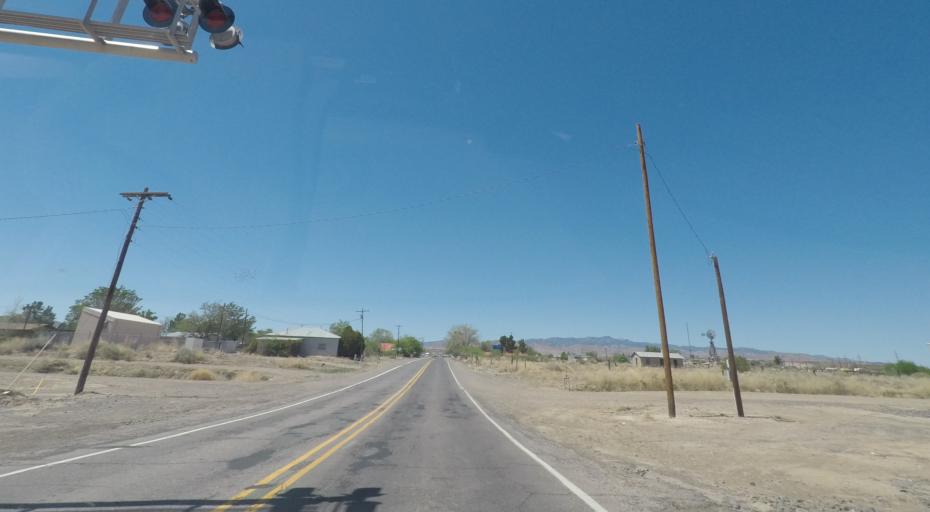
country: US
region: New Mexico
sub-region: Socorro County
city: Socorro
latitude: 33.9181
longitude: -106.8634
